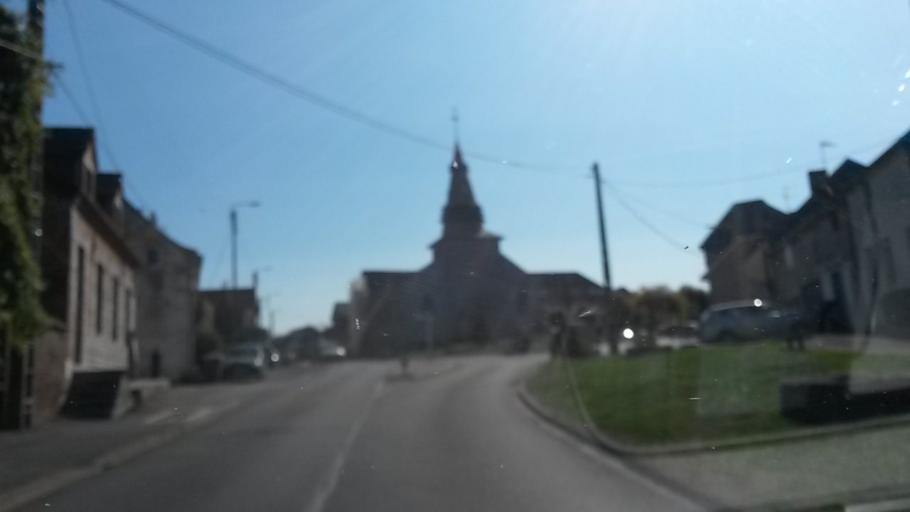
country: FR
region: Nord-Pas-de-Calais
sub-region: Departement du Nord
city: Avesnelles
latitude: 50.1186
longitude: 3.9456
